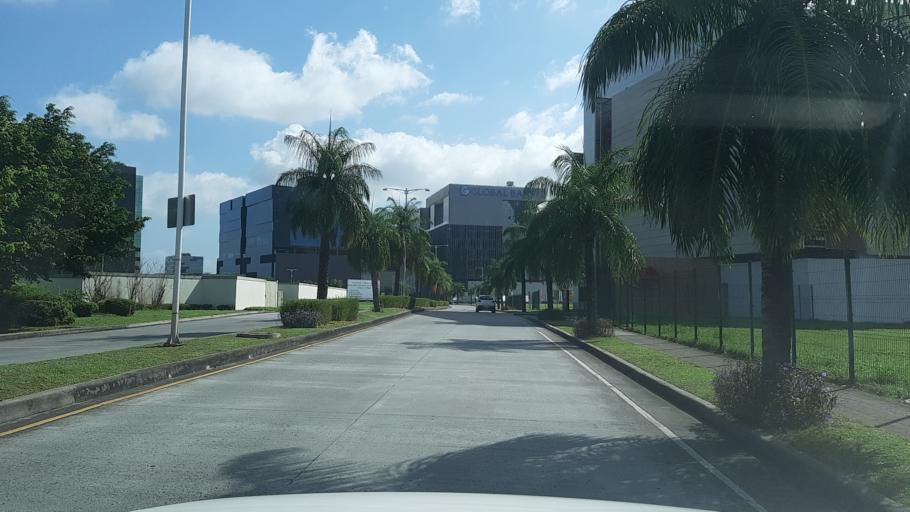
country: PA
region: Panama
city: San Miguelito
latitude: 9.0277
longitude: -79.4650
